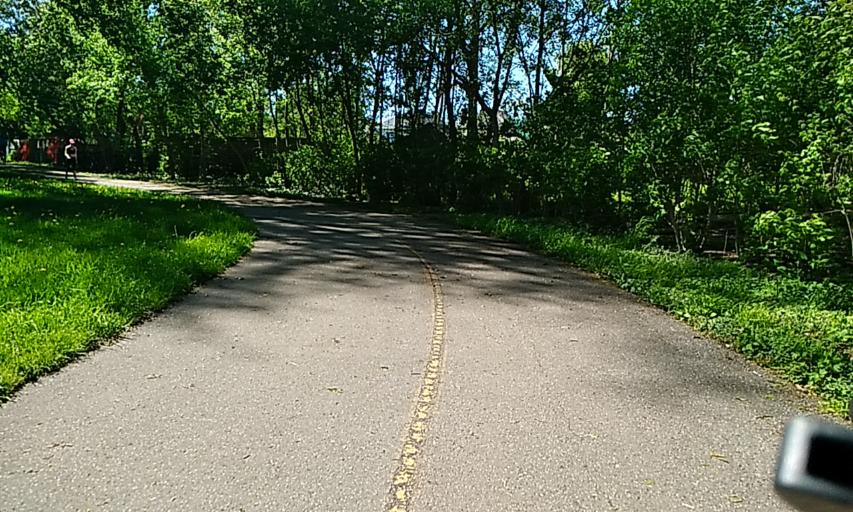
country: CA
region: Ontario
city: London
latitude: 42.9761
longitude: -81.2441
